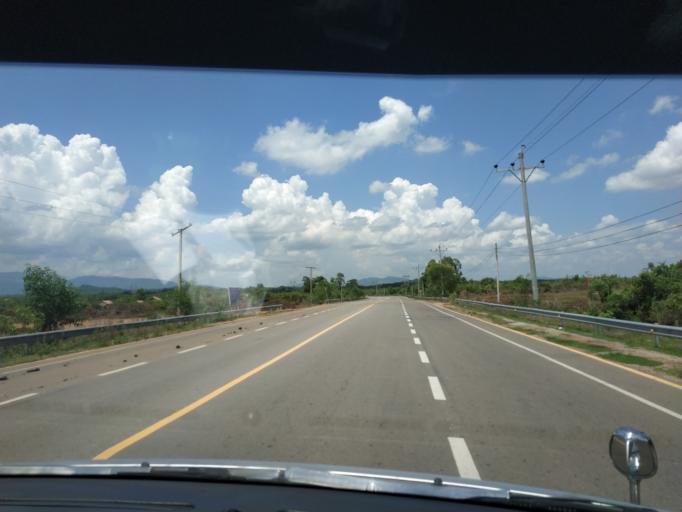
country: MM
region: Mon
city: Kyaikto
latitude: 17.3306
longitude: 97.0303
